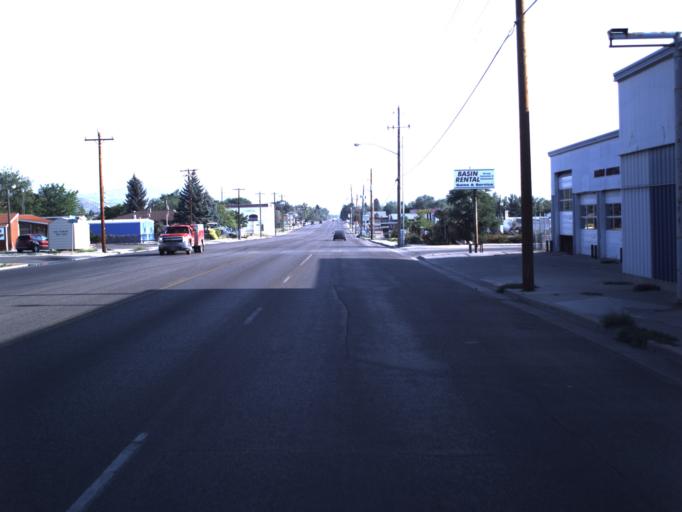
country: US
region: Utah
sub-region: Uintah County
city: Vernal
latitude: 40.4595
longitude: -109.5286
